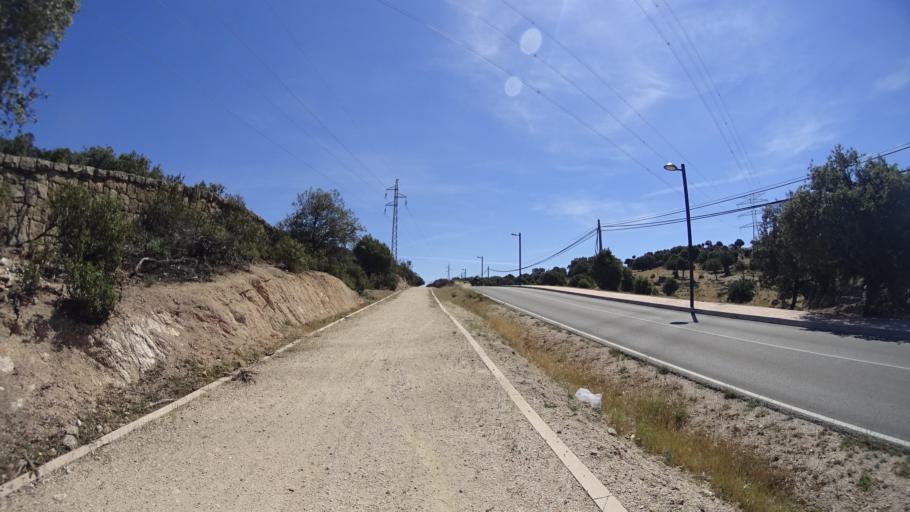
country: ES
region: Madrid
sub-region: Provincia de Madrid
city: Hoyo de Manzanares
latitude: 40.6152
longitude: -3.9264
